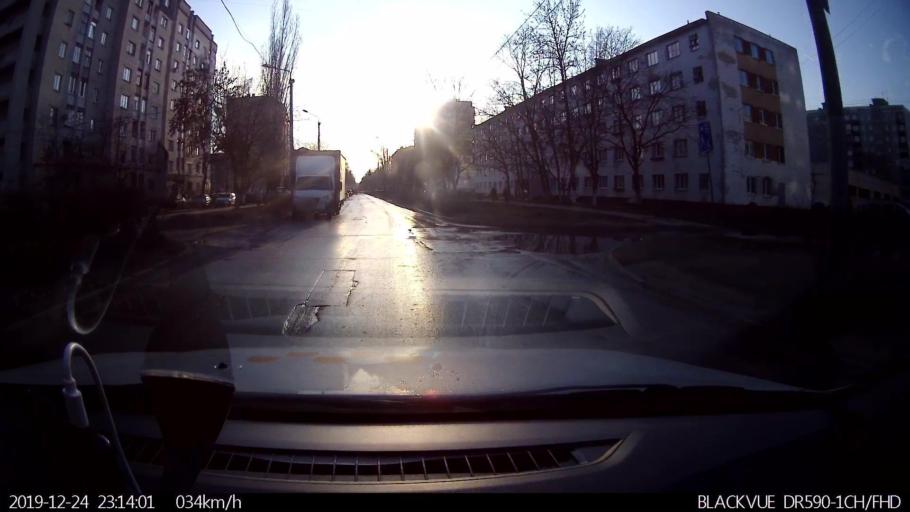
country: RU
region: Nizjnij Novgorod
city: Gorbatovka
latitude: 56.2515
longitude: 43.8585
